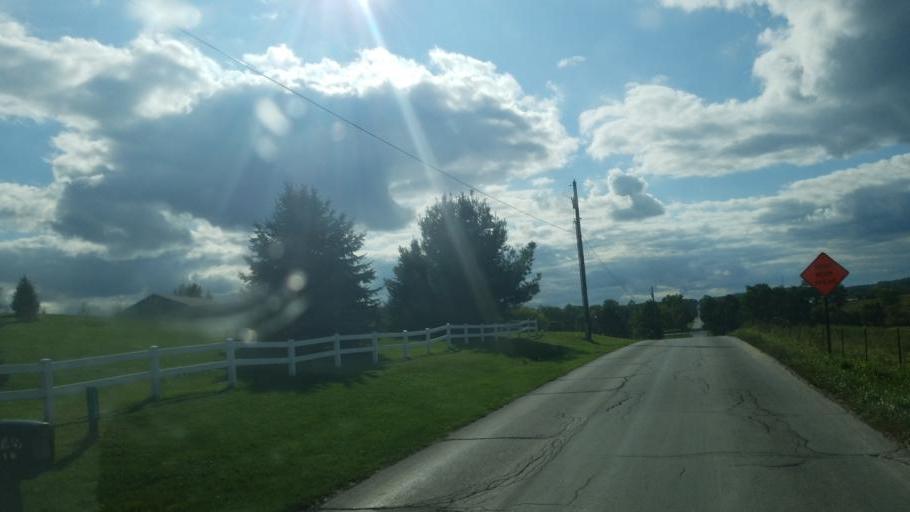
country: US
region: Ohio
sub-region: Sandusky County
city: Bellville
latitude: 40.5864
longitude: -82.5732
